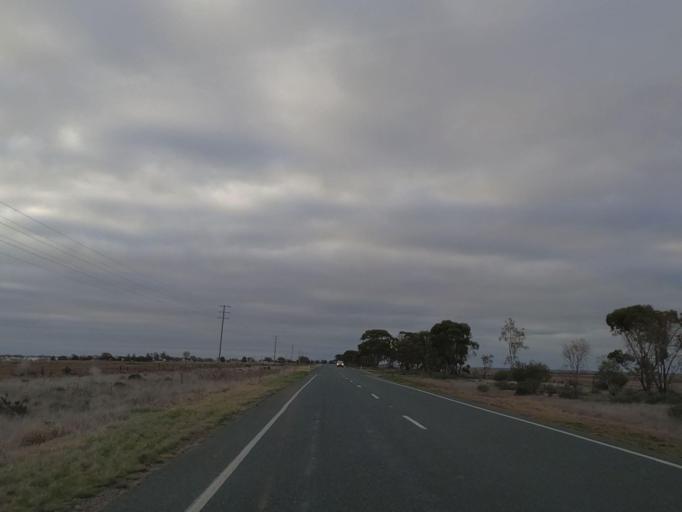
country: AU
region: Victoria
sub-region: Swan Hill
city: Swan Hill
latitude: -35.5912
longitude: 143.7905
